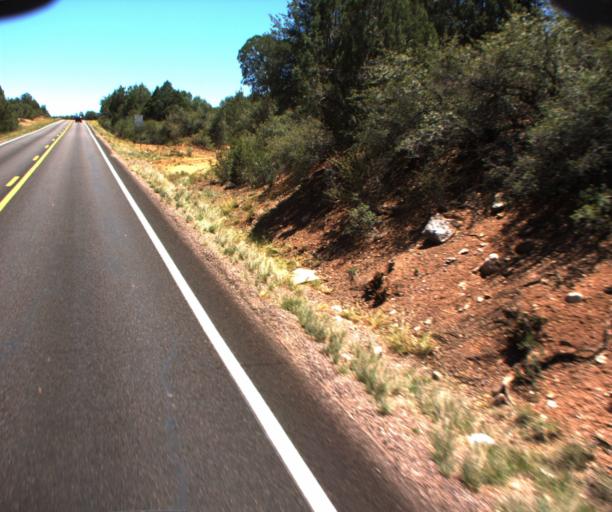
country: US
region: Arizona
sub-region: Gila County
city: Payson
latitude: 34.2909
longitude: -111.3461
